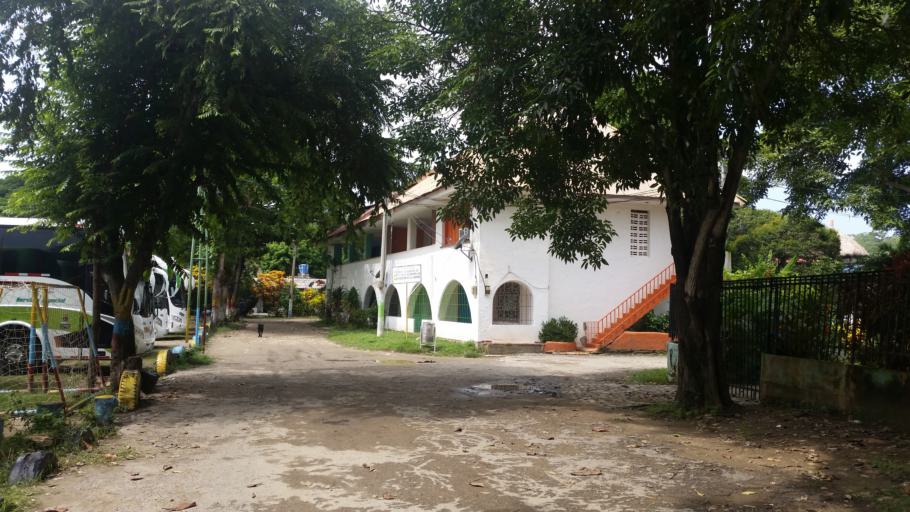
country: CO
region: Magdalena
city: Santa Marta
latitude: 11.2609
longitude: -73.7693
